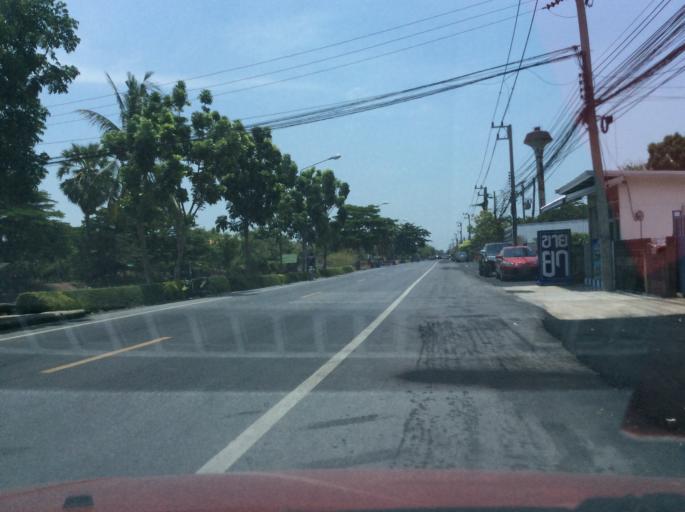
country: TH
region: Pathum Thani
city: Lam Luk Ka
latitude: 13.9487
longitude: 100.7270
